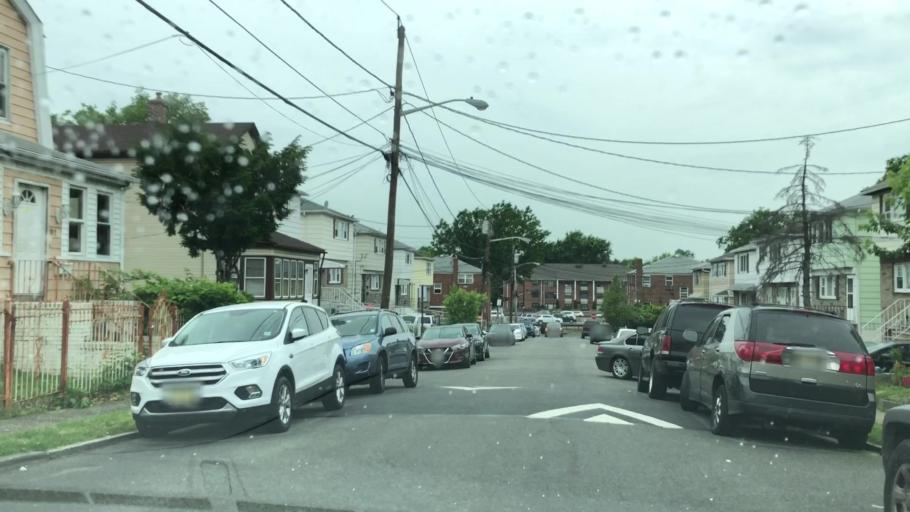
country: US
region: New Jersey
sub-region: Essex County
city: Irvington
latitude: 40.7324
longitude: -74.2193
